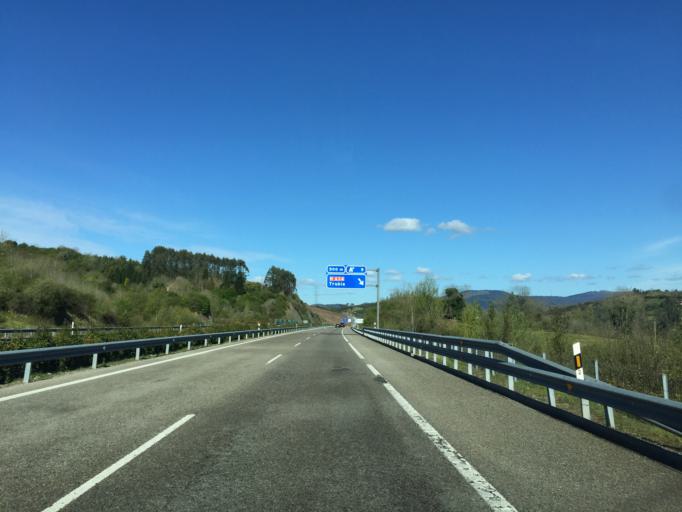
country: ES
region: Asturias
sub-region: Province of Asturias
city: Castandiello
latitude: 43.3563
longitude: -5.9395
